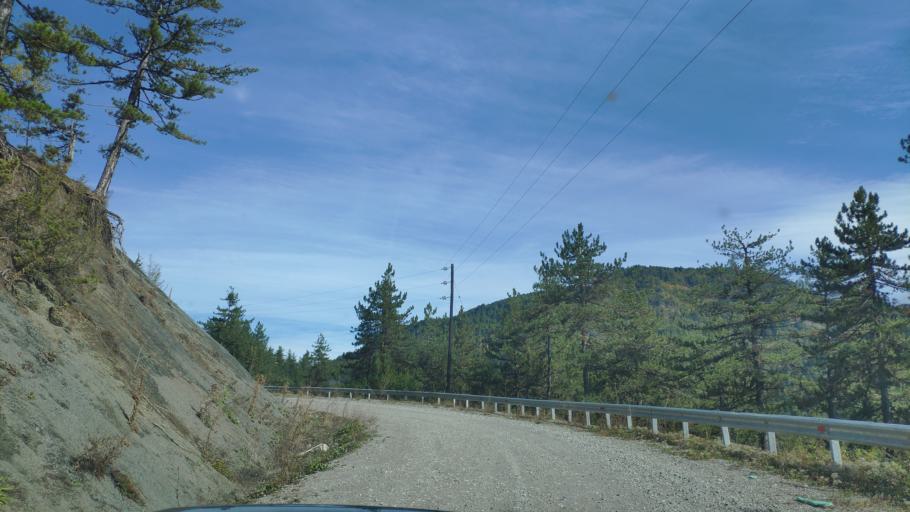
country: AL
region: Korce
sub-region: Rrethi i Devollit
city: Miras
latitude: 40.4158
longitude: 20.8706
